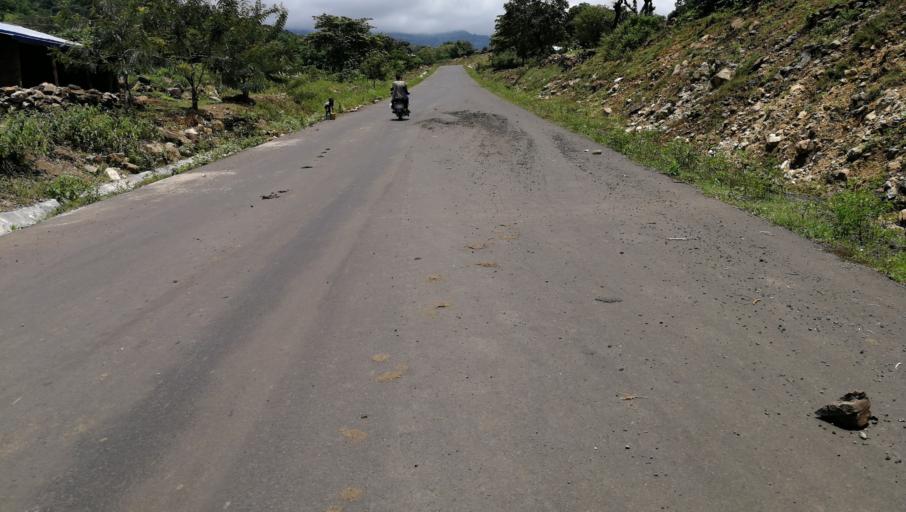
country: ET
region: Southern Nations, Nationalities, and People's Region
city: Areka
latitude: 6.9210
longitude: 37.2971
